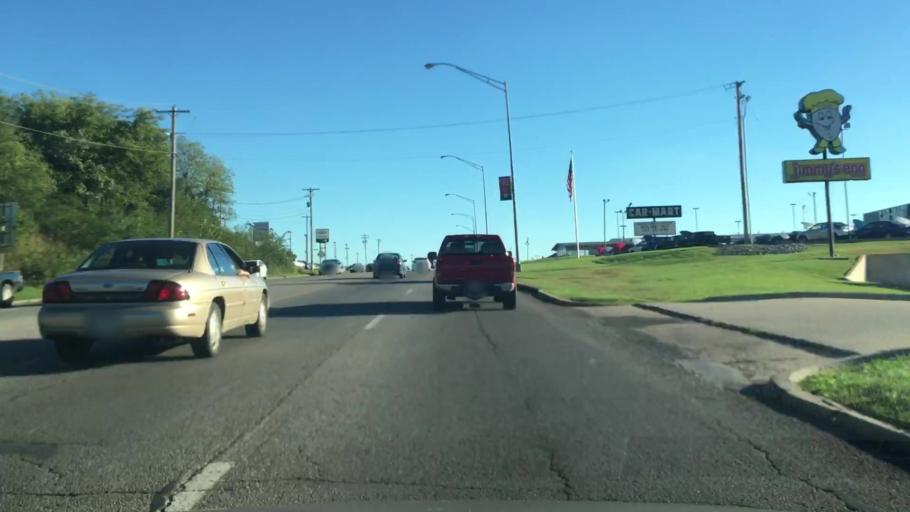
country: US
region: Oklahoma
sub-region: Cherokee County
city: Park Hill
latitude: 35.8846
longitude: -94.9766
